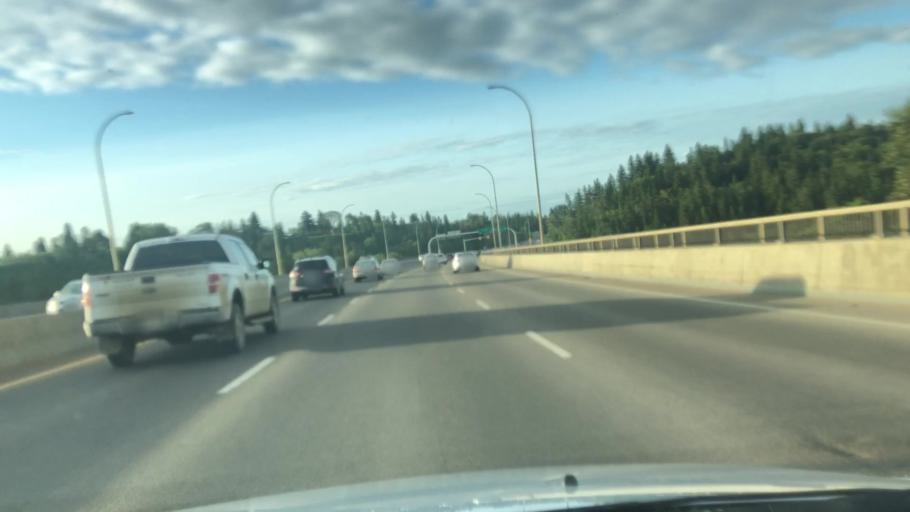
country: CA
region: Alberta
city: Edmonton
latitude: 53.5569
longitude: -113.4393
